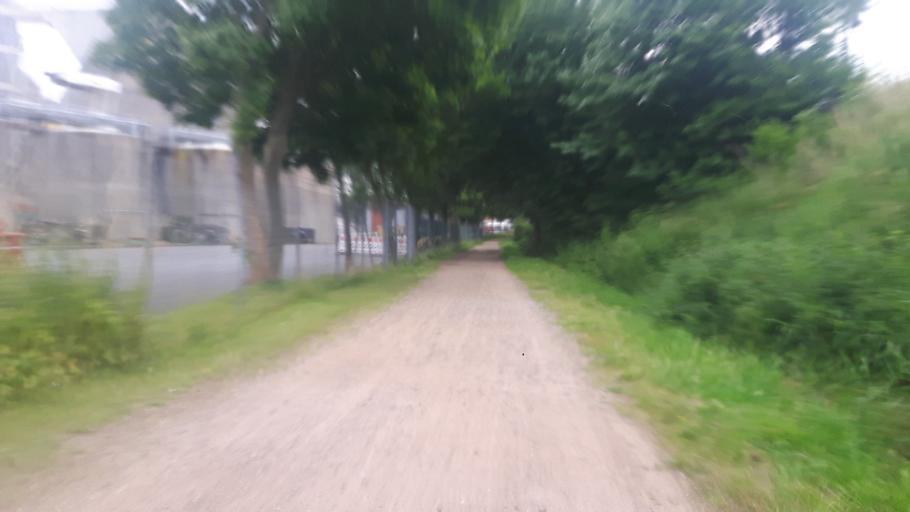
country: DE
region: Schleswig-Holstein
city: Bad Schwartau
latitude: 53.9004
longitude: 10.6932
